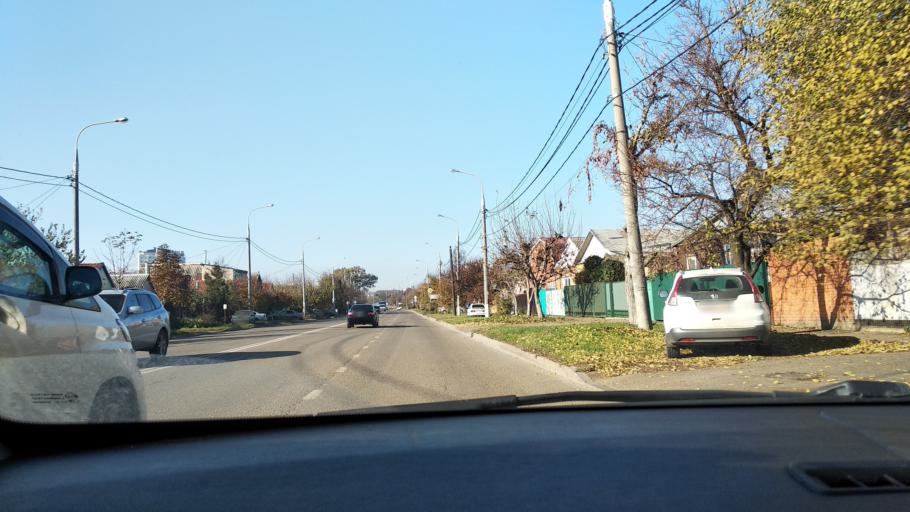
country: RU
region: Krasnodarskiy
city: Krasnodar
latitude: 45.0144
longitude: 39.0024
